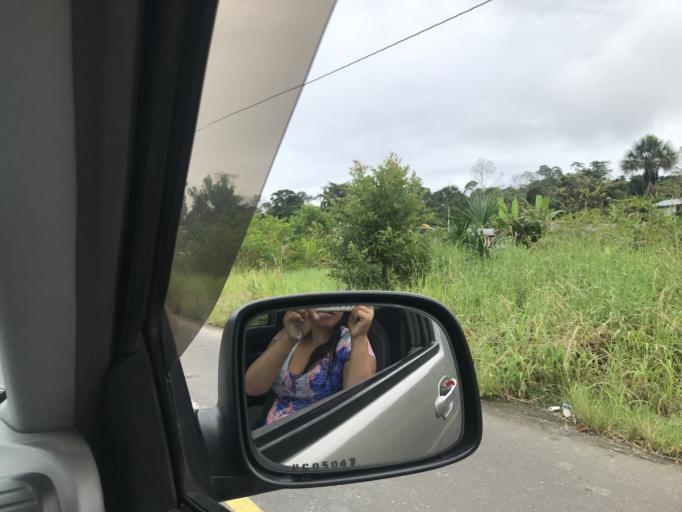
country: EC
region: Napo
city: Tena
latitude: -1.0561
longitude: -77.8159
